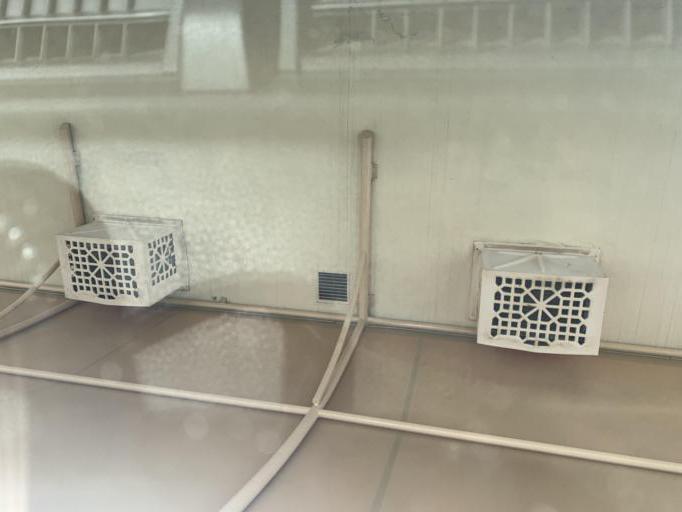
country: BH
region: Manama
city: Manama
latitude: 26.2105
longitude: 50.5817
